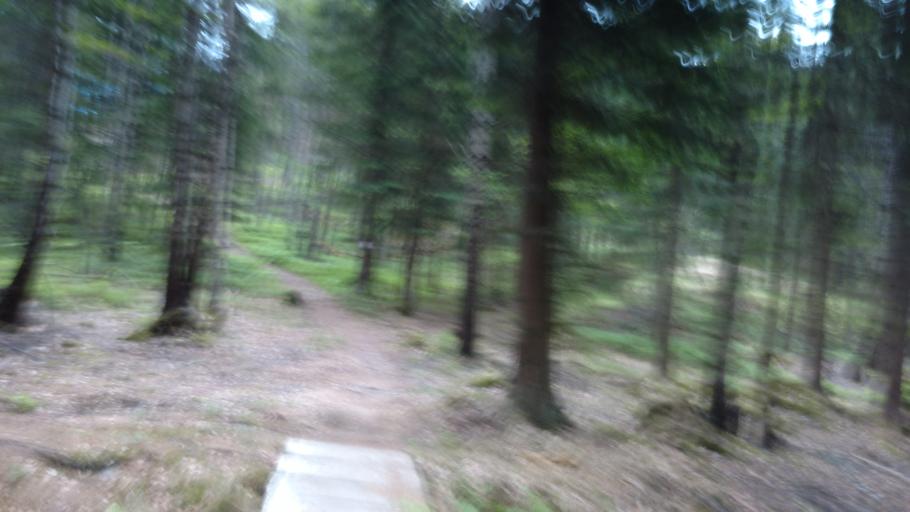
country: FI
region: Uusimaa
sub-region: Raaseporin
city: Pohja
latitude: 60.1186
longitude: 23.5515
